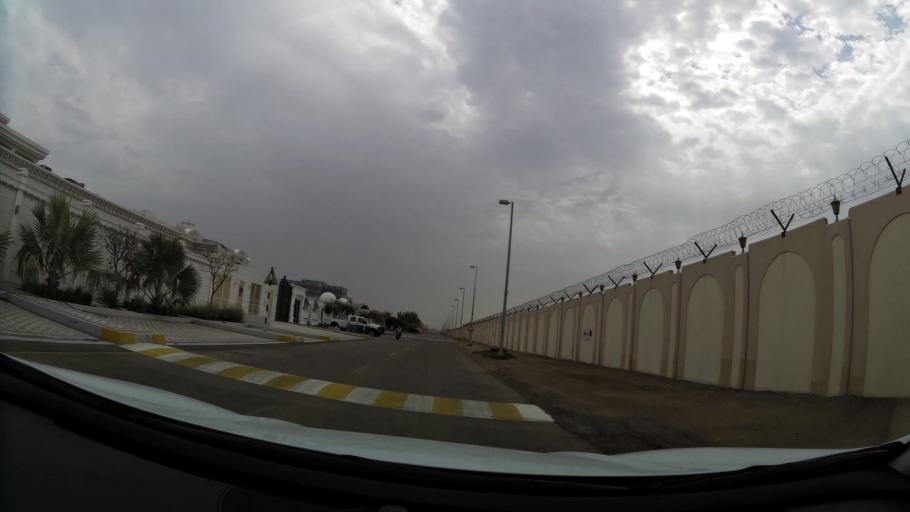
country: AE
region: Abu Dhabi
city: Abu Dhabi
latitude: 24.4381
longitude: 54.4472
